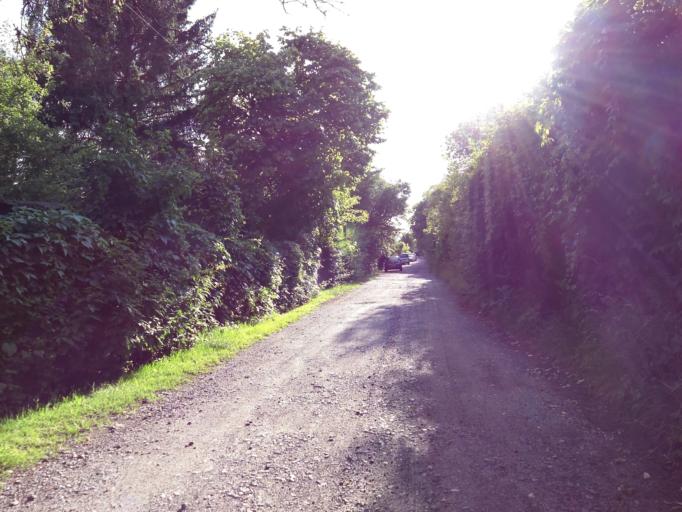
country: DE
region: Saxony
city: Taucha
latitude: 51.3398
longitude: 12.4434
